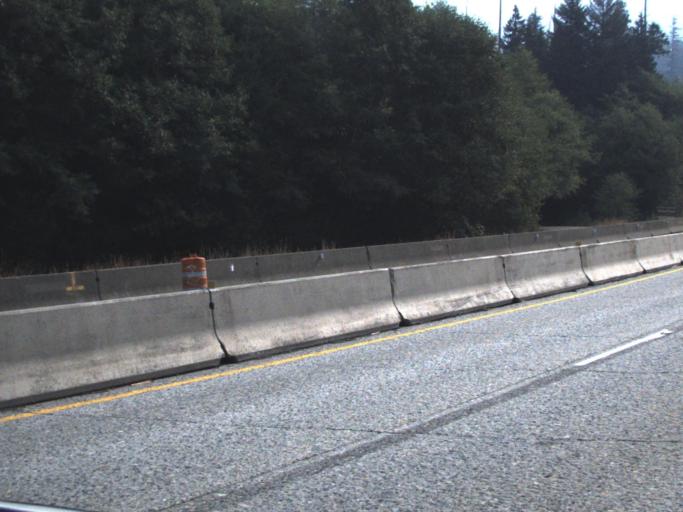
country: US
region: Washington
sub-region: King County
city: Tanner
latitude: 47.3931
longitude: -121.4722
